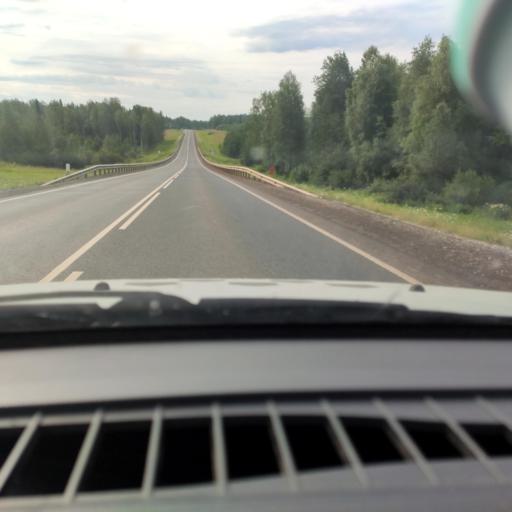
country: RU
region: Perm
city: Siva
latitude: 58.6335
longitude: 53.8582
